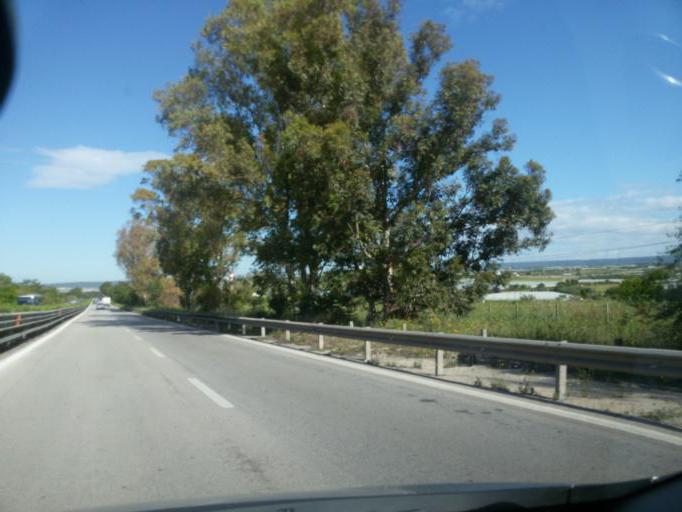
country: IT
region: Apulia
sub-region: Provincia di Taranto
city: Grottaglie
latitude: 40.5280
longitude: 17.4146
